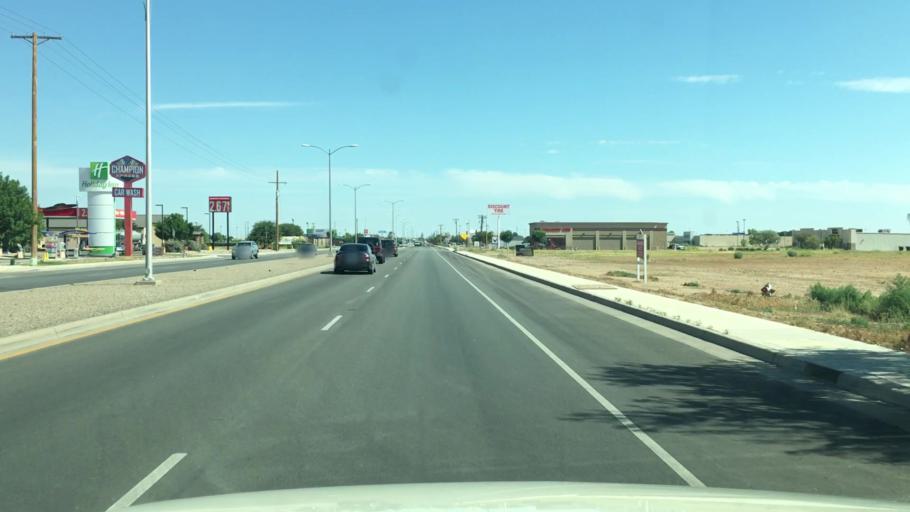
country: US
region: New Mexico
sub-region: Chaves County
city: Roswell
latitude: 33.4422
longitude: -104.5232
